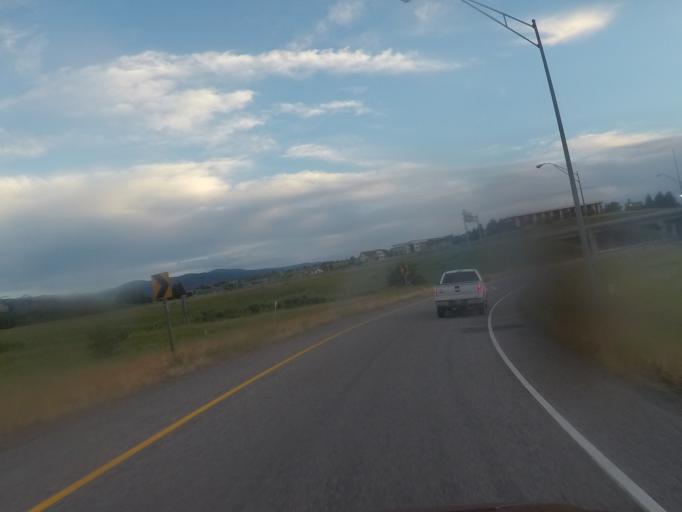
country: US
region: Montana
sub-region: Gallatin County
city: Bozeman
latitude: 45.6758
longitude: -111.0088
